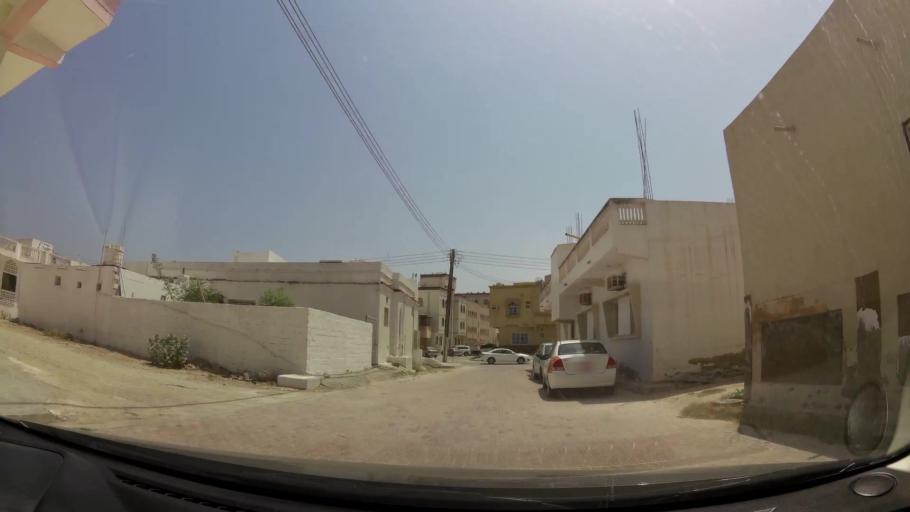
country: OM
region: Zufar
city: Salalah
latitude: 17.0152
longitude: 54.0793
